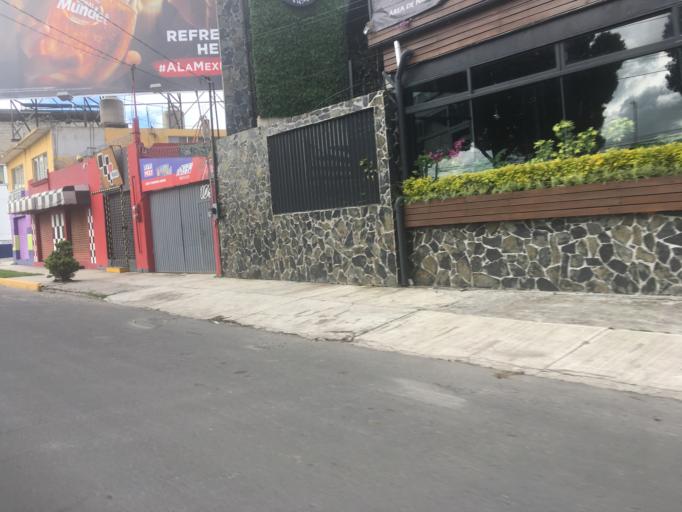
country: MX
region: Morelos
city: Metepec
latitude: 19.2822
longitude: -99.6092
